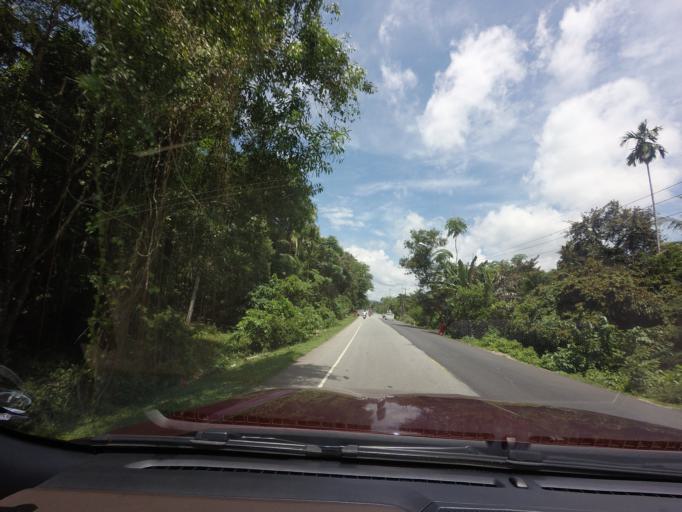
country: TH
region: Narathiwat
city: Ra-ngae
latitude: 6.2569
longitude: 101.6880
